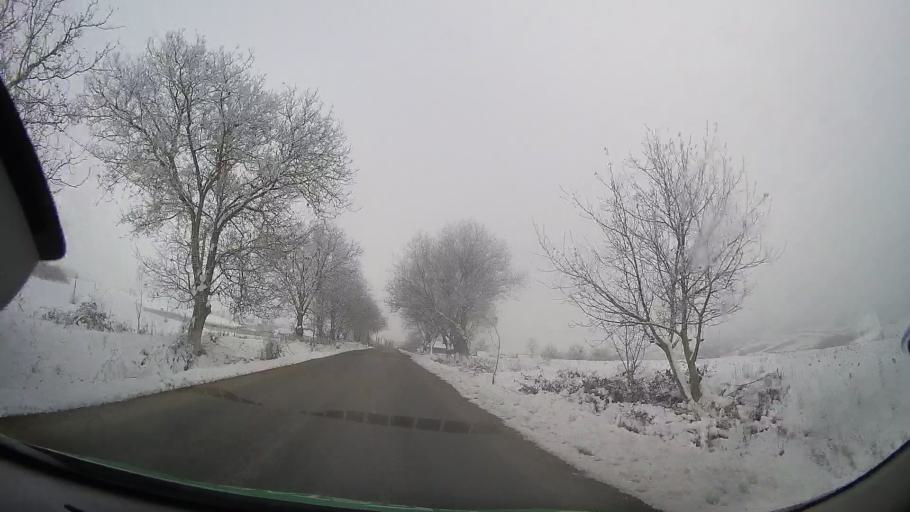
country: RO
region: Bacau
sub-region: Comuna Oncesti
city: Oncesti
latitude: 46.4460
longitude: 27.2646
